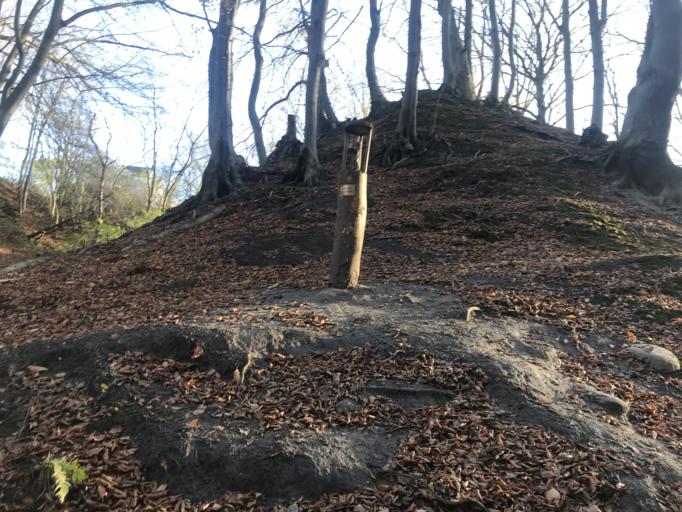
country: PL
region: Pomeranian Voivodeship
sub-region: Powiat pucki
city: Jastrzebia Gora
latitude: 54.8333
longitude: 18.3269
